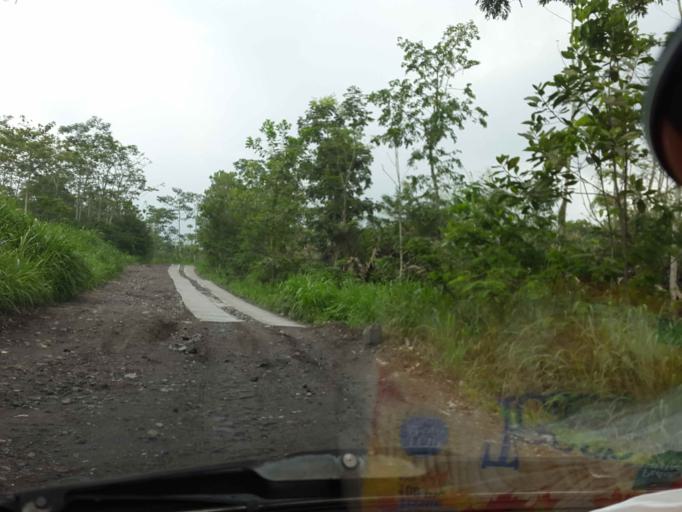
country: ID
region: Central Java
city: Muntilan
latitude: -7.5864
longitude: 110.3783
